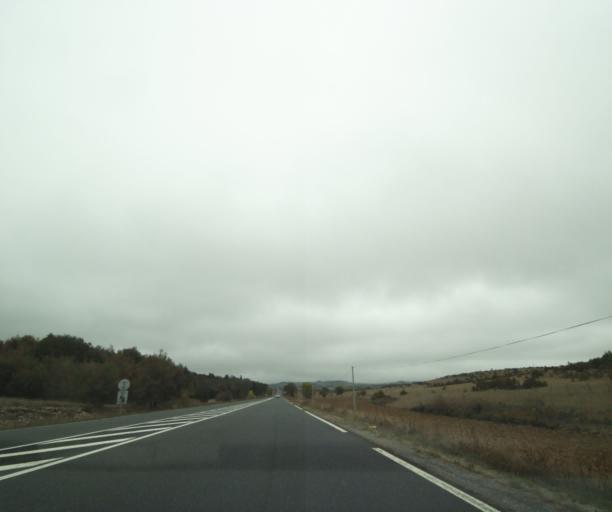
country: FR
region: Midi-Pyrenees
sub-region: Departement de l'Aveyron
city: La Cavalerie
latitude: 44.0325
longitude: 3.1473
